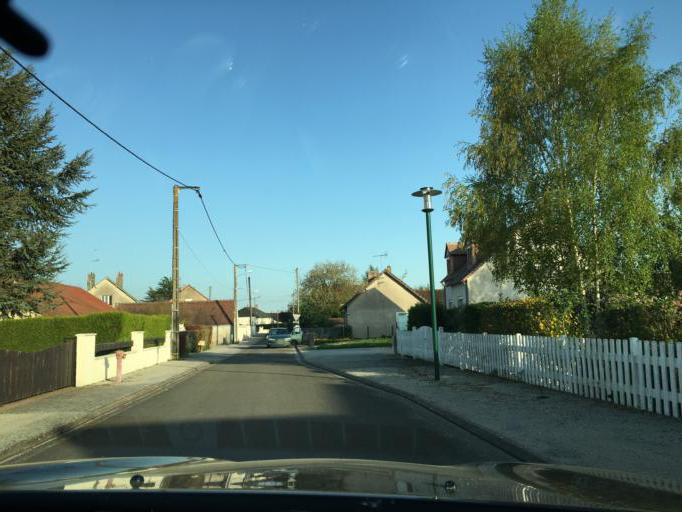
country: FR
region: Centre
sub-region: Departement du Loir-et-Cher
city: Ouzouer-le-Marche
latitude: 47.9077
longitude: 1.5243
